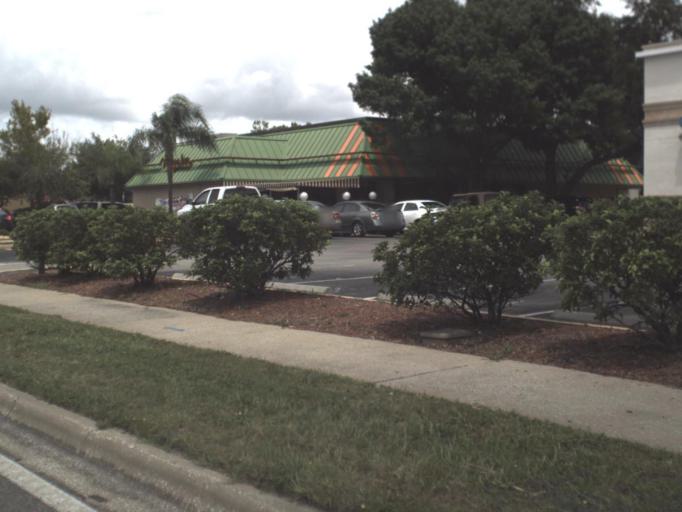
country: US
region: Florida
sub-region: Hillsborough County
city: Town 'n' Country
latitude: 27.9967
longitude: -82.5583
